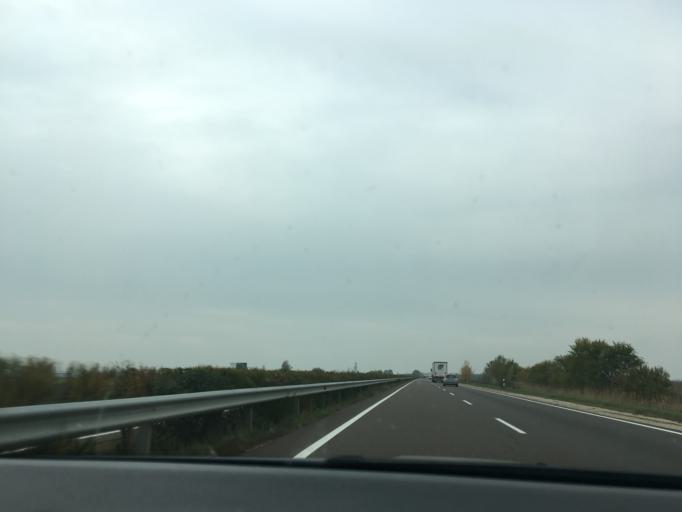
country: HU
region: Pest
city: Cegled
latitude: 47.1924
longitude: 19.8450
